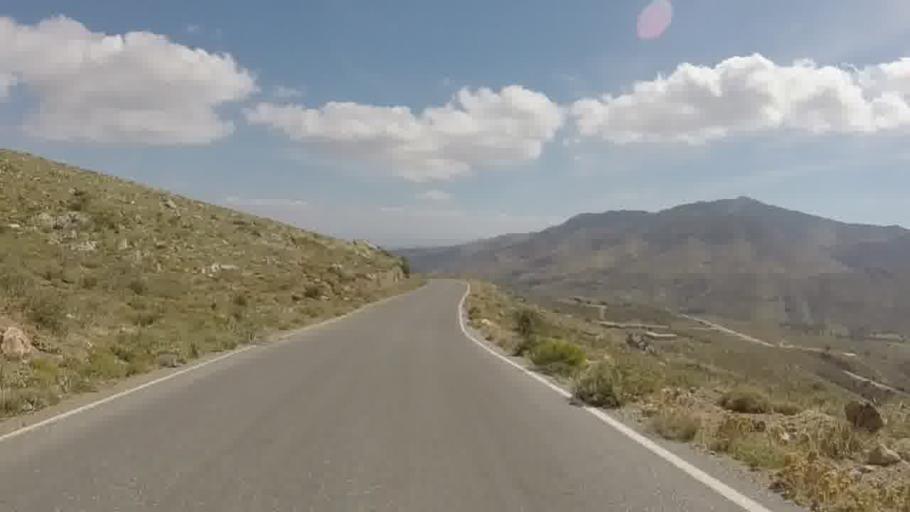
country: GR
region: Crete
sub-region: Nomos Rethymnis
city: Agia Galini
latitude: 35.1562
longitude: 24.6174
